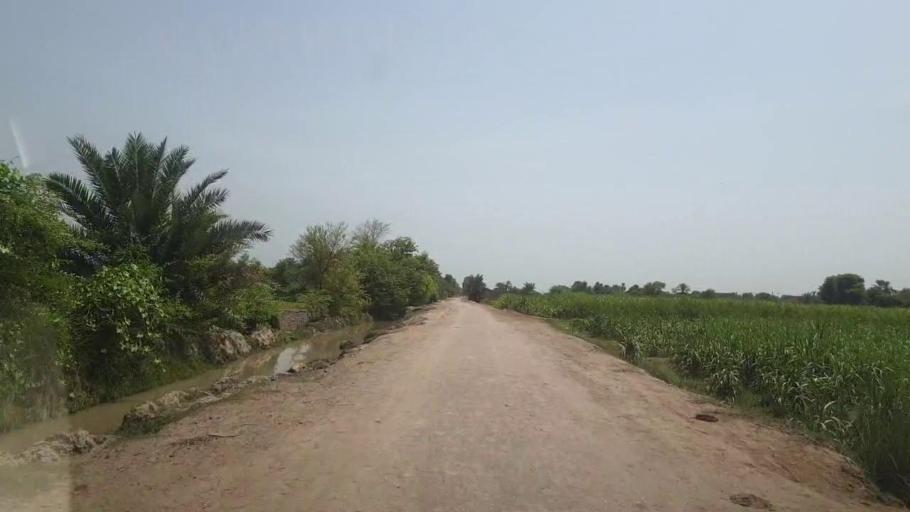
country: PK
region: Sindh
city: Sobhadero
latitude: 27.4413
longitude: 68.4030
